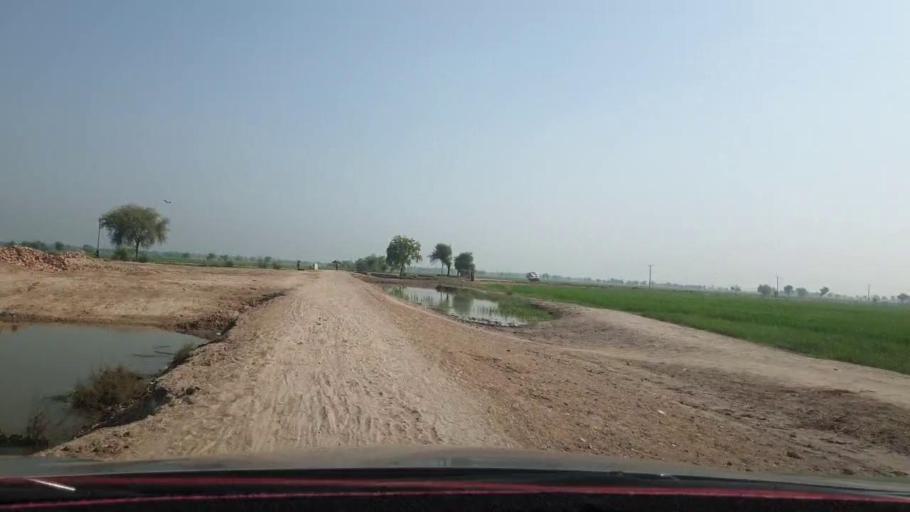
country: PK
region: Sindh
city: Kambar
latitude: 27.4965
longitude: 67.9306
